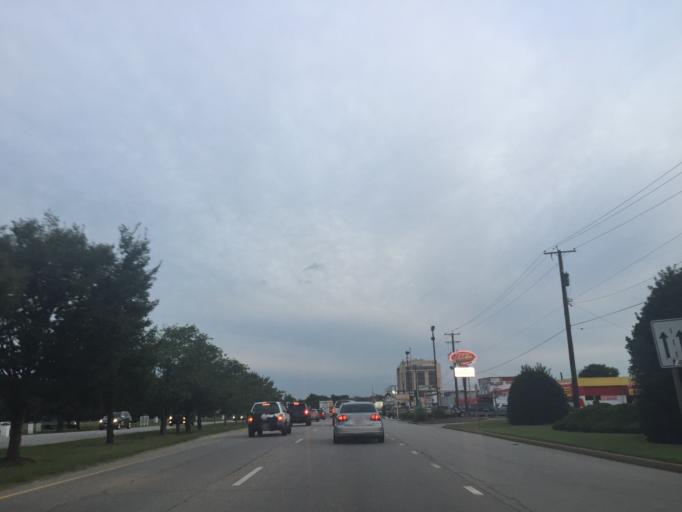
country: US
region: Maryland
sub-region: Anne Arundel County
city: Glen Burnie
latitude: 39.1755
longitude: -76.6176
